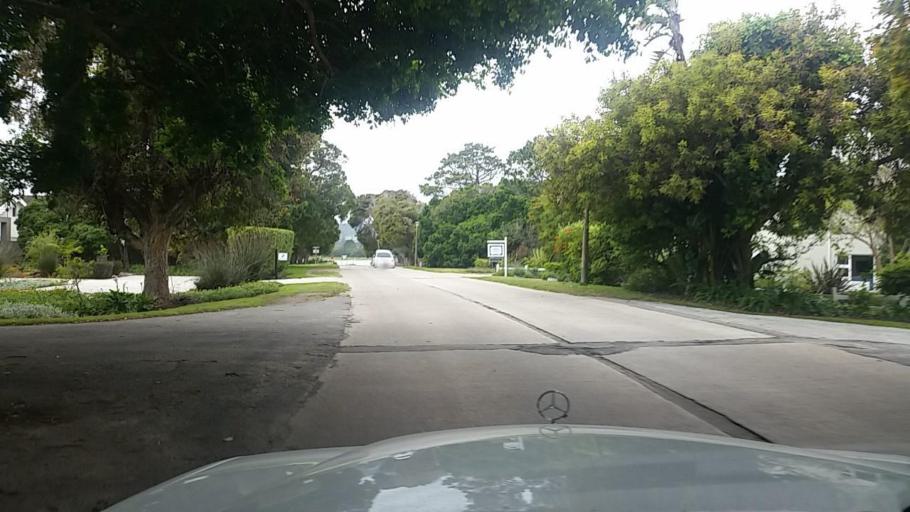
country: ZA
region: Western Cape
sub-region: Eden District Municipality
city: Knysna
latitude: -34.0672
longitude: 23.0631
